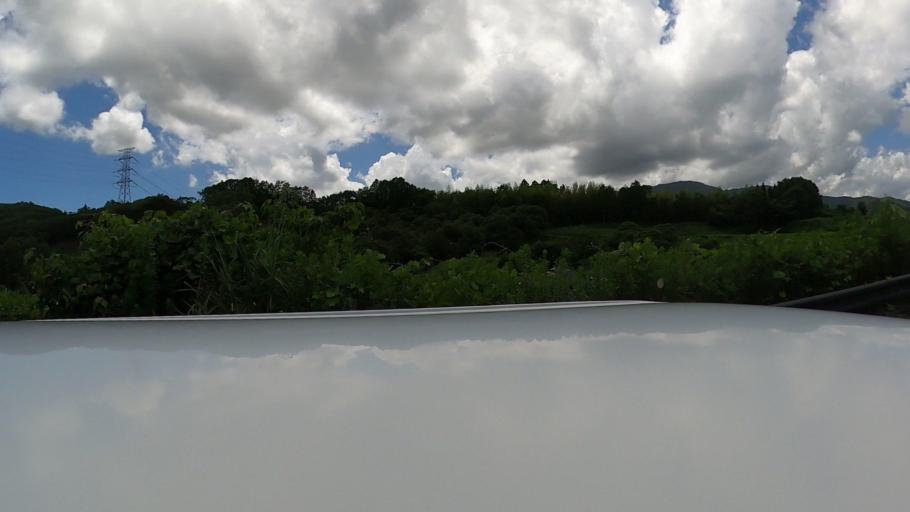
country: JP
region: Miyazaki
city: Nobeoka
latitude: 32.5817
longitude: 131.5181
